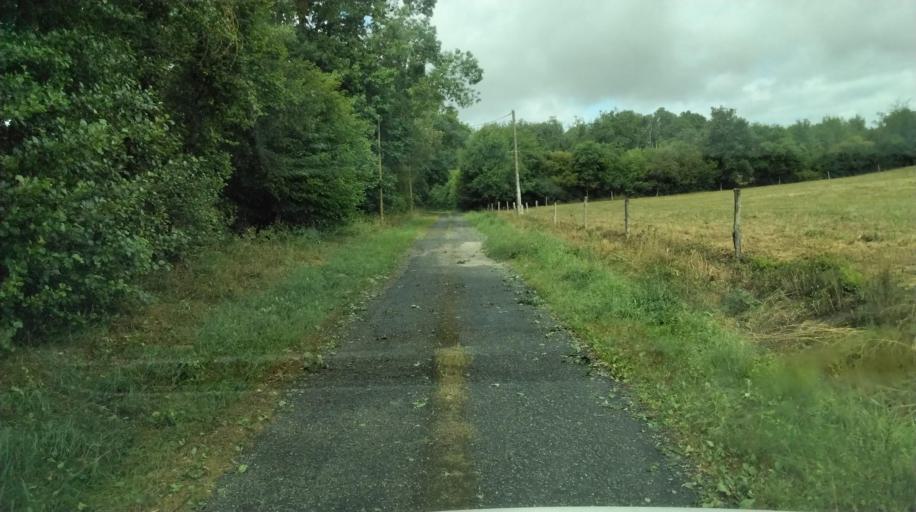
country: FR
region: Midi-Pyrenees
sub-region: Departement de la Haute-Garonne
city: Rieumes
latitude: 43.4224
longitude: 1.1603
